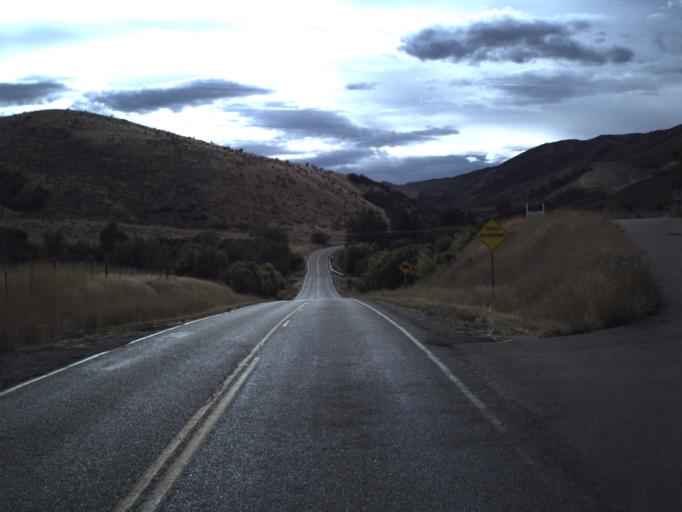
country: US
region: Utah
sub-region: Morgan County
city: Morgan
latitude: 40.9512
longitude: -111.6600
